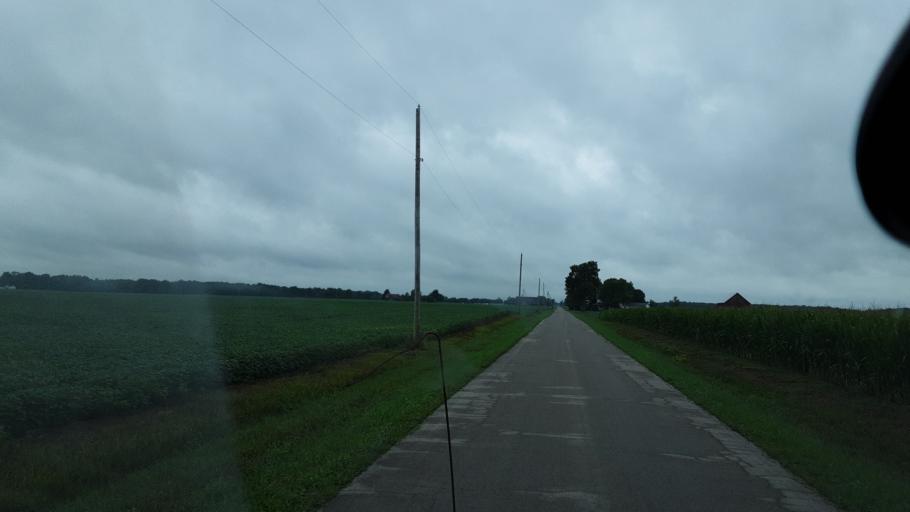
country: US
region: Ohio
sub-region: Van Wert County
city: Convoy
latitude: 40.8297
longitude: -84.7636
